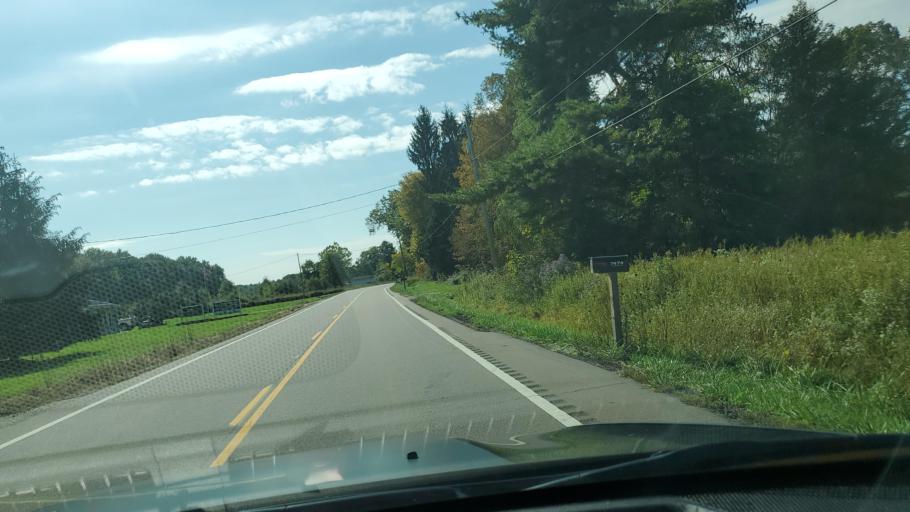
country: US
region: Ohio
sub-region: Trumbull County
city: Cortland
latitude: 41.4242
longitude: -80.6006
